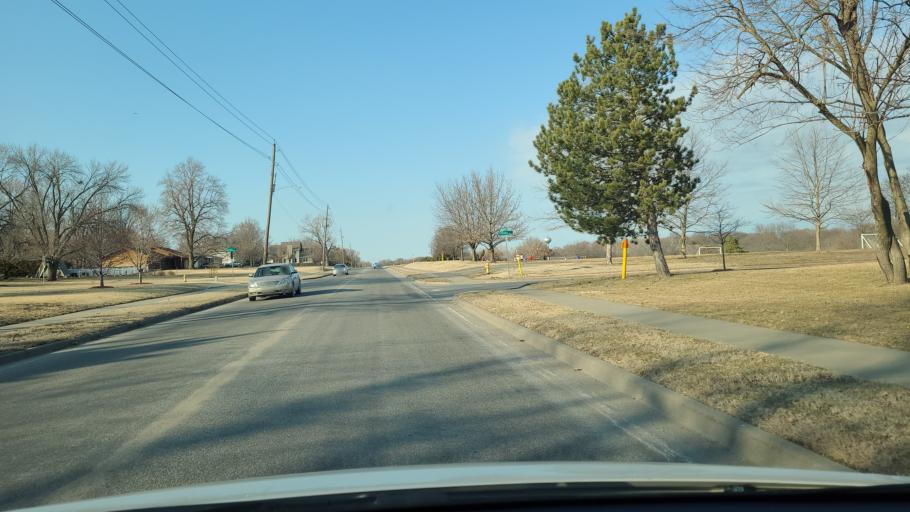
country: US
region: Kansas
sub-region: Douglas County
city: Lawrence
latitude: 38.9596
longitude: -95.2883
